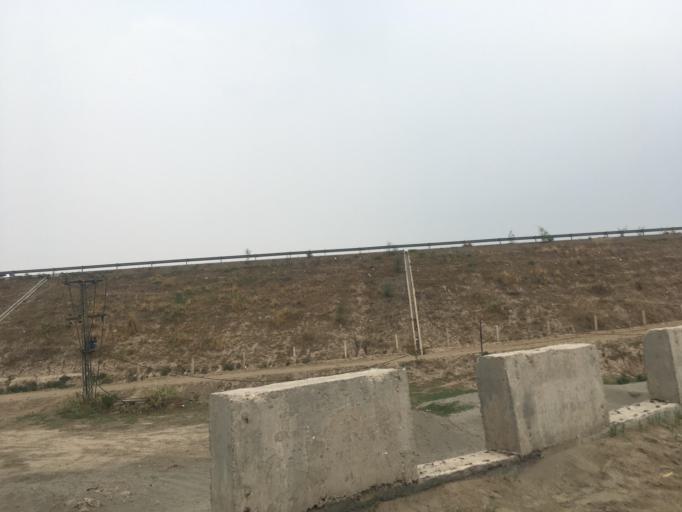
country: PK
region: Punjab
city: Lahore
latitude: 31.6356
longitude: 74.3541
